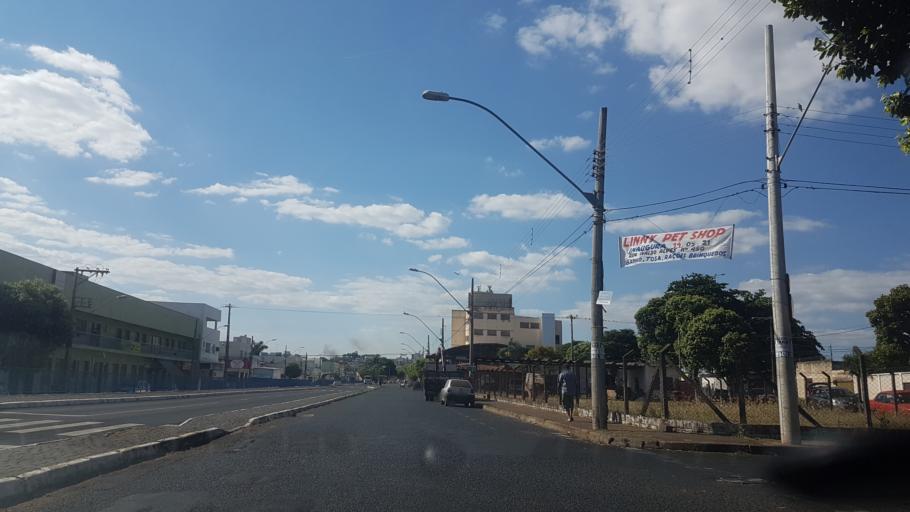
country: BR
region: Minas Gerais
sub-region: Uberlandia
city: Uberlandia
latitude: -18.9023
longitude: -48.2716
